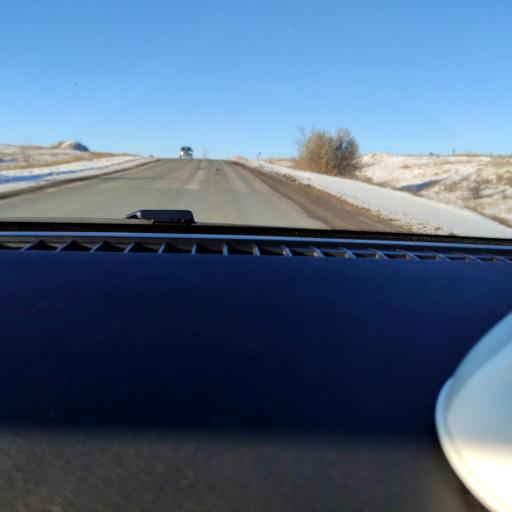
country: RU
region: Samara
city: Spiridonovka
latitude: 53.1444
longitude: 50.5848
